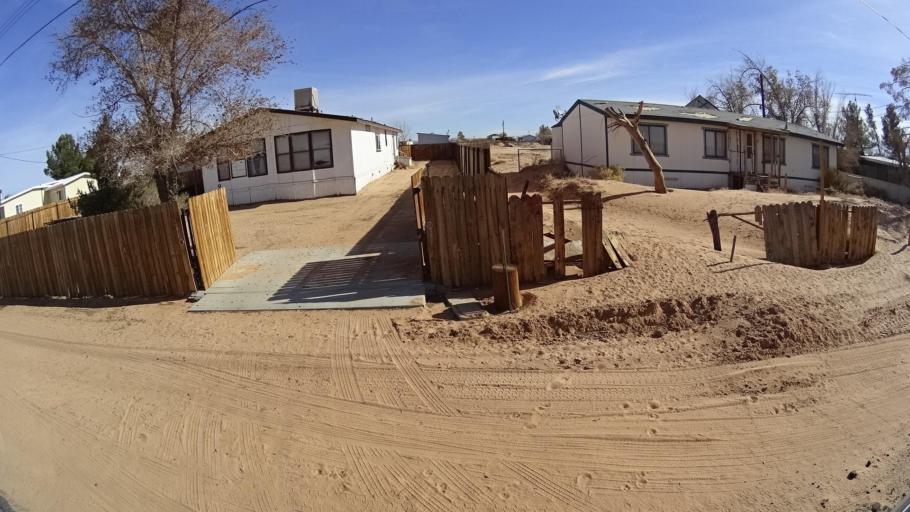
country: US
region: California
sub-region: Kern County
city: North Edwards
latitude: 35.0914
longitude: -117.7927
